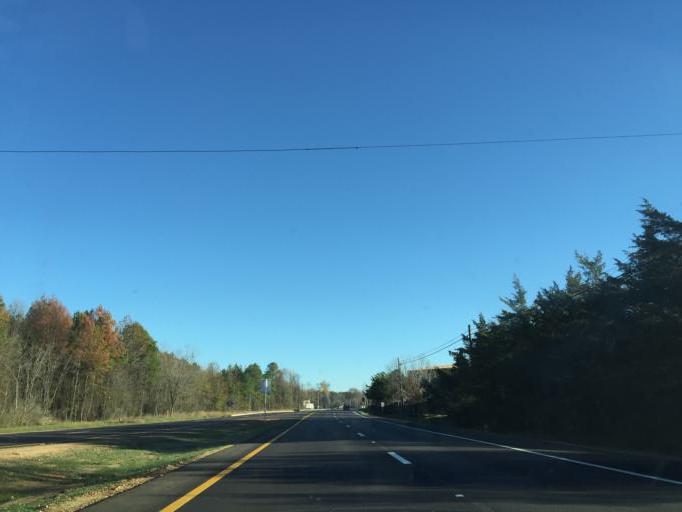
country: US
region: Mississippi
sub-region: Rankin County
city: Flowood
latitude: 32.3130
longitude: -90.1385
